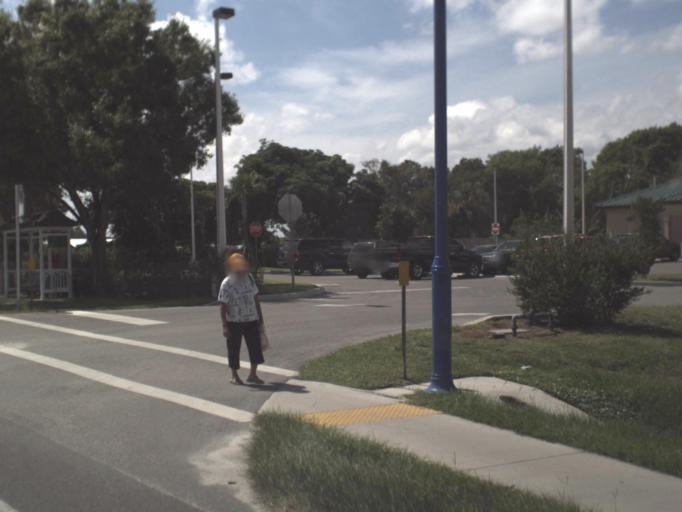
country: US
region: Florida
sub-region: Collier County
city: Immokalee
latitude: 26.4247
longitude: -81.4337
